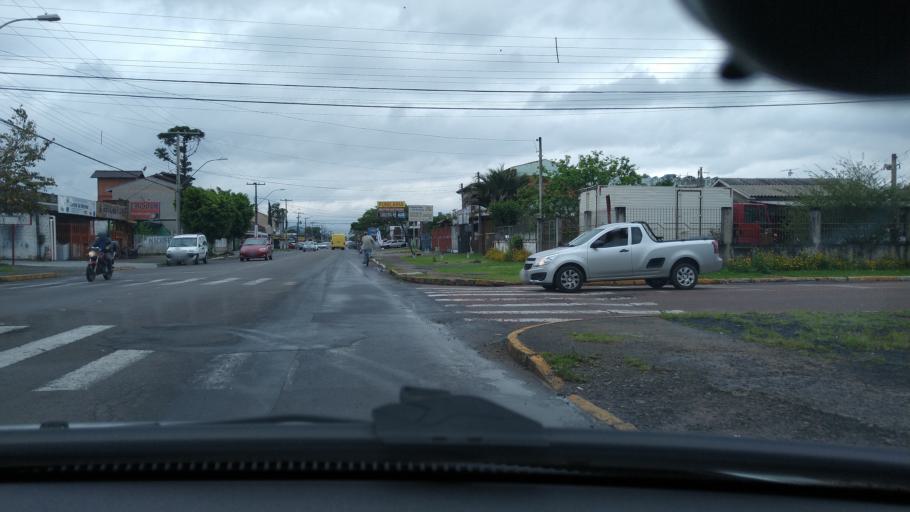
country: BR
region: Rio Grande do Sul
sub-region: Canoas
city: Canoas
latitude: -29.9016
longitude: -51.2119
